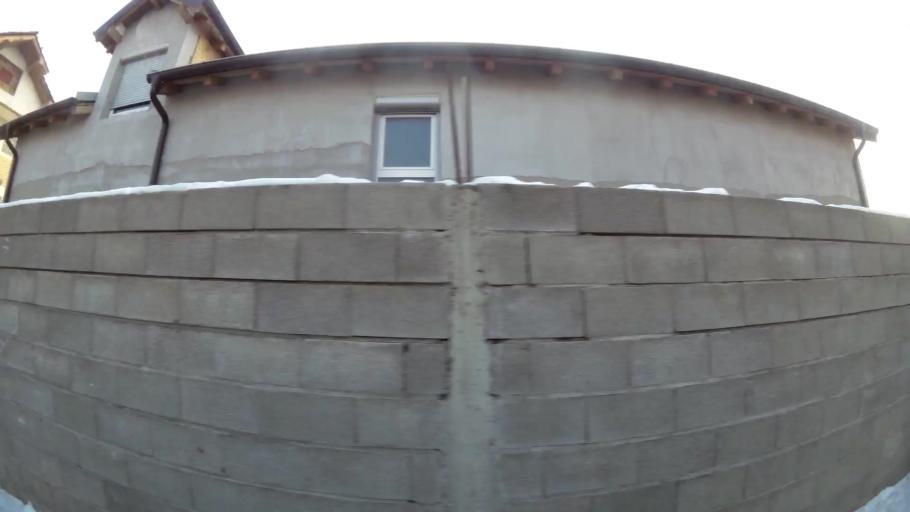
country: MK
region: Aracinovo
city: Arachinovo
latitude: 42.0125
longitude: 21.5285
